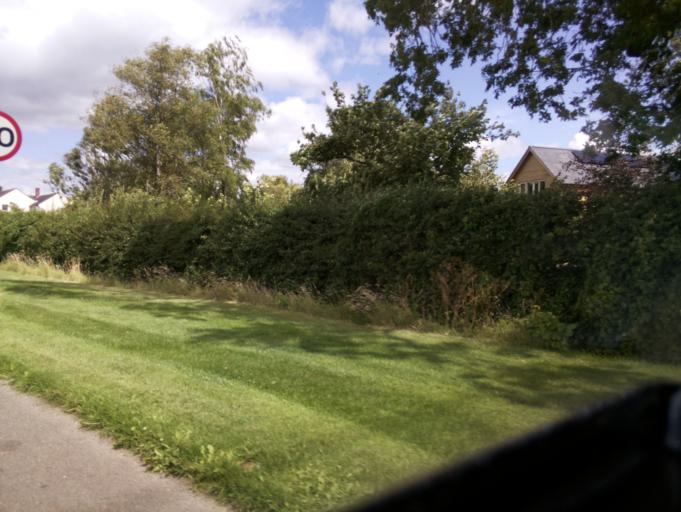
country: GB
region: England
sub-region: Nottinghamshire
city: Cotgrave
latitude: 52.8664
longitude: -1.0722
